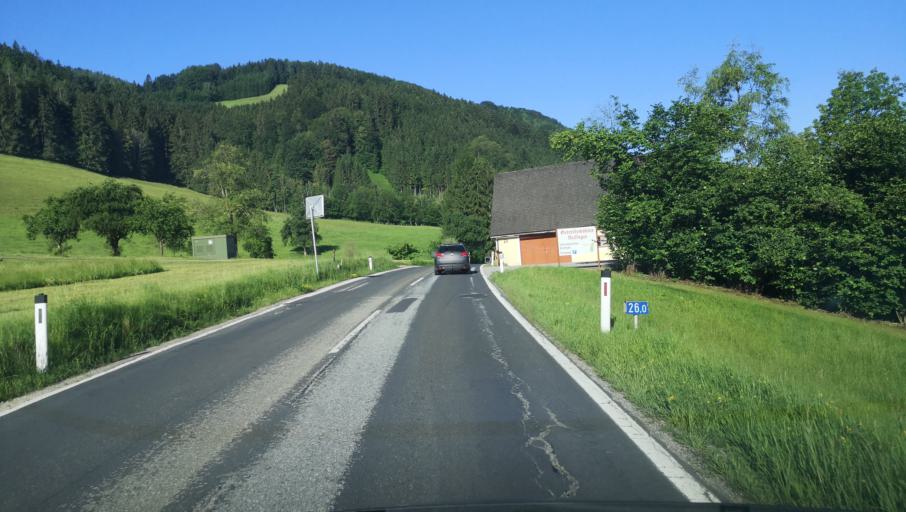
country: AT
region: Lower Austria
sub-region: Politischer Bezirk Amstetten
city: Ybbsitz
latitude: 47.9390
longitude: 14.8516
